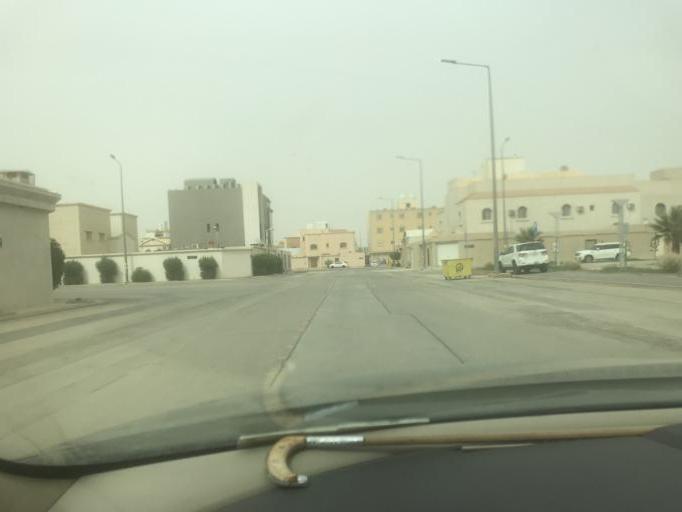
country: SA
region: Ar Riyad
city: Riyadh
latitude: 24.7311
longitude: 46.7941
